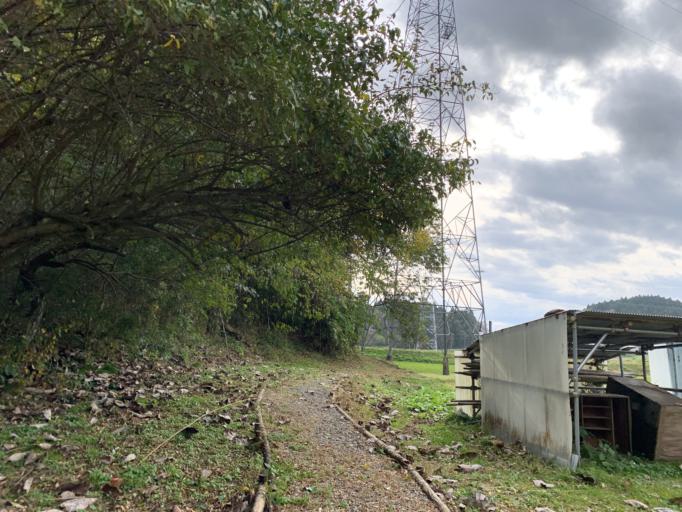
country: JP
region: Iwate
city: Mizusawa
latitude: 39.0257
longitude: 141.1348
